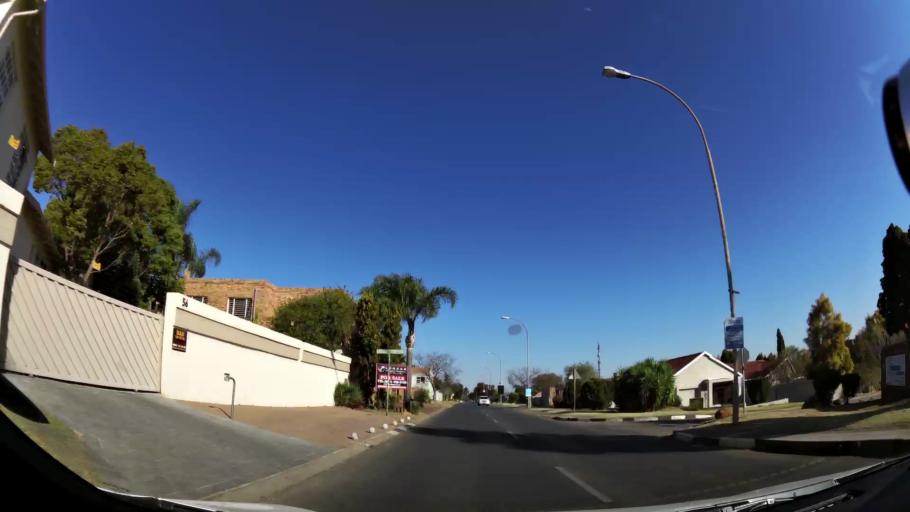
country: ZA
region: Gauteng
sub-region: City of Johannesburg Metropolitan Municipality
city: Johannesburg
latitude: -26.2950
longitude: 28.0539
